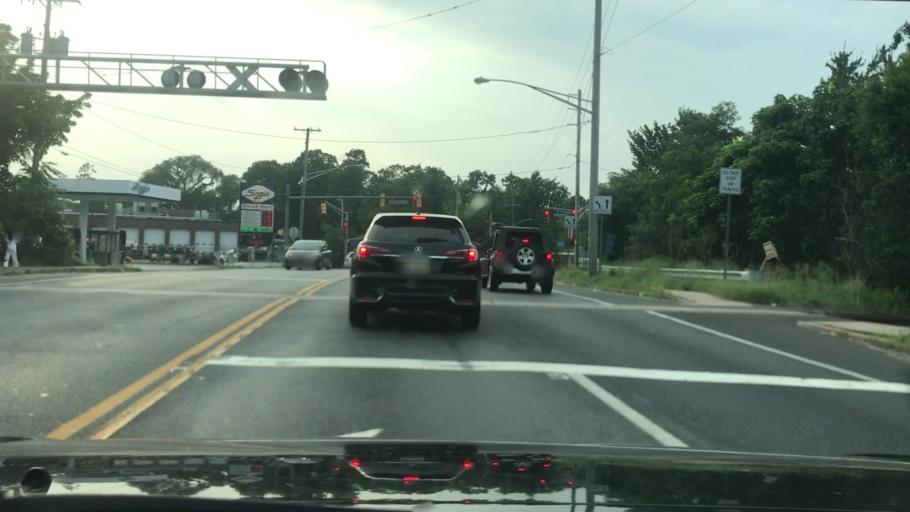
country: US
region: New Jersey
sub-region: Ocean County
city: Lakewood
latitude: 40.0873
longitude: -74.2128
